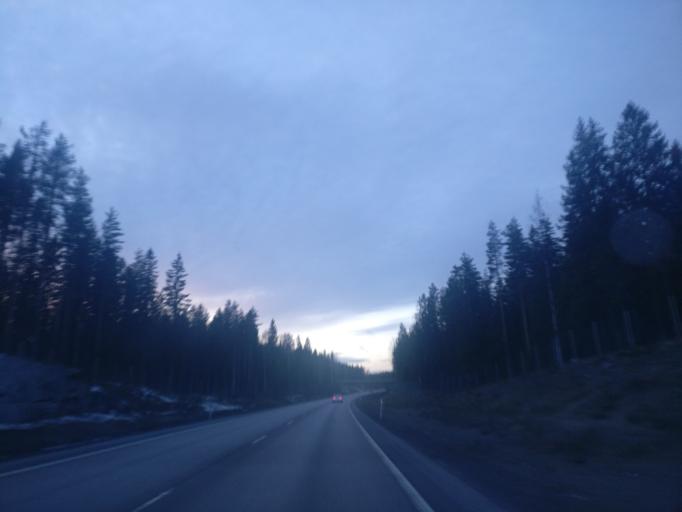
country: FI
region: Central Finland
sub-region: Jyvaeskylae
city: Saeynaetsalo
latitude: 62.1954
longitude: 25.8962
